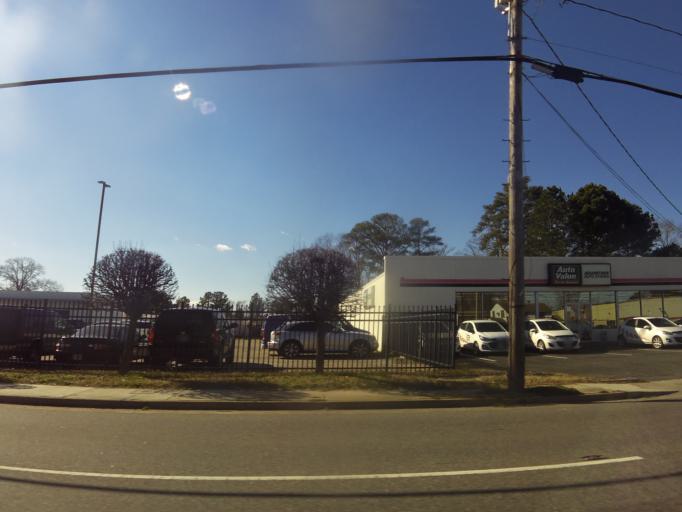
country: US
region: Virginia
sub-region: City of Newport News
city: Newport News
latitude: 37.0136
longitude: -76.4410
